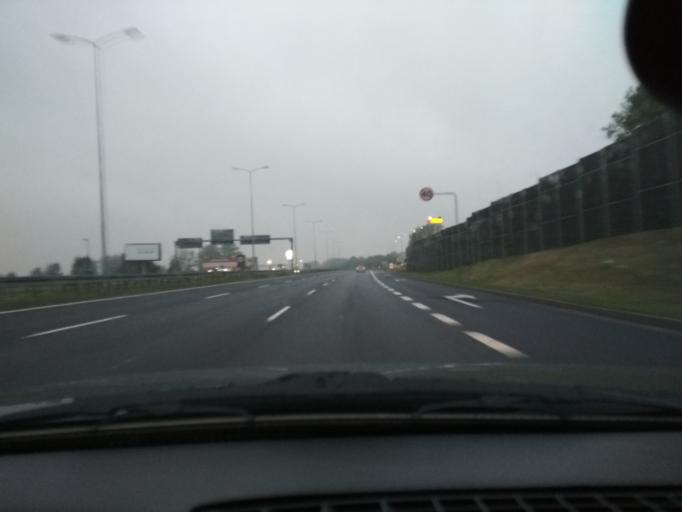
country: PL
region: Silesian Voivodeship
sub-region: Ruda Slaska
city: Ruda Slaska
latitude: 50.2988
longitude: 18.8515
